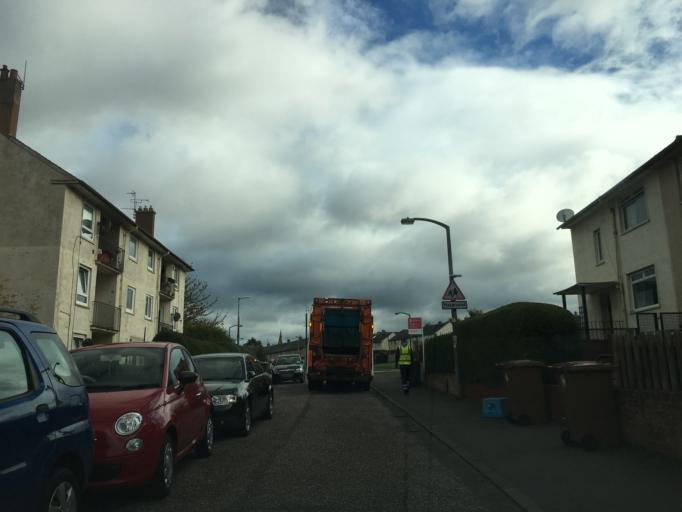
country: GB
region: Scotland
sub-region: Midlothian
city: Loanhead
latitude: 55.9176
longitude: -3.1607
